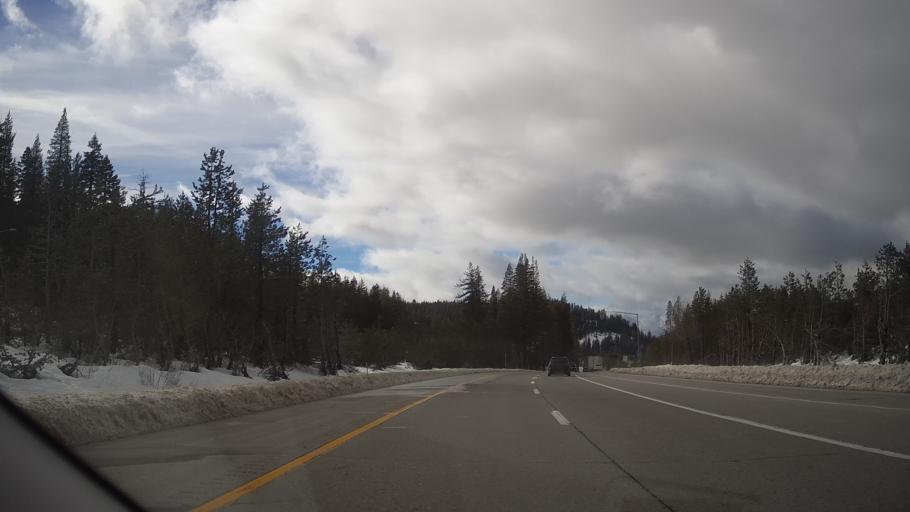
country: US
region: California
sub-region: Nevada County
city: Truckee
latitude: 39.3246
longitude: -120.3947
